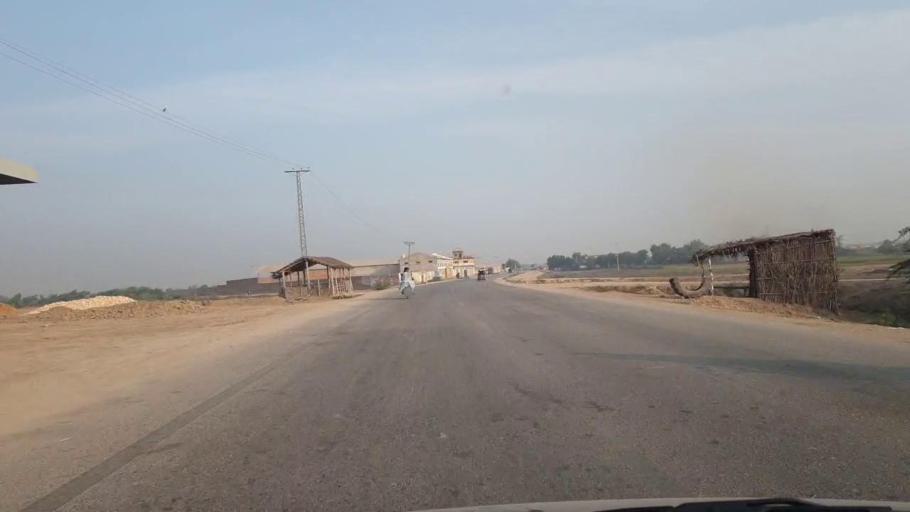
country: PK
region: Sindh
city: Badin
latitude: 24.6845
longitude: 68.8243
